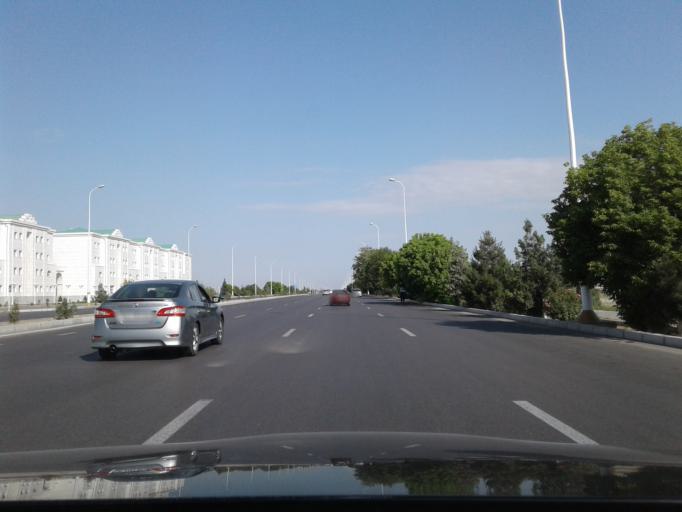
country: TM
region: Ahal
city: Ashgabat
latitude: 37.9930
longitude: 58.3149
